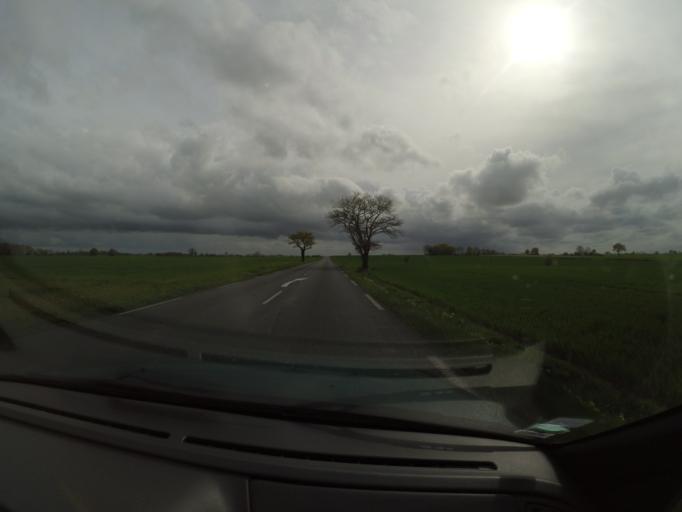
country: FR
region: Pays de la Loire
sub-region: Departement de Maine-et-Loire
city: Saint-Laurent-des-Autels
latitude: 47.2556
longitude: -1.2050
